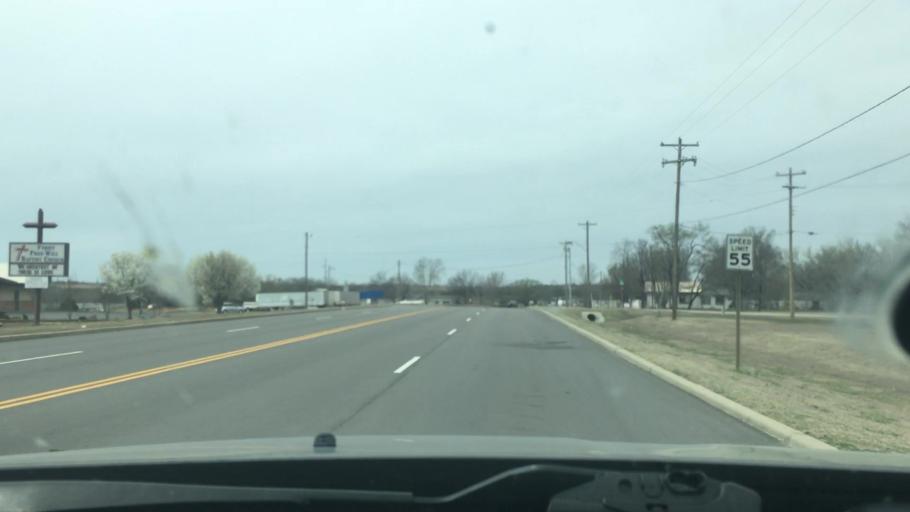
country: US
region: Oklahoma
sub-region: Seminole County
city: Seminole
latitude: 35.2604
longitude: -96.7124
